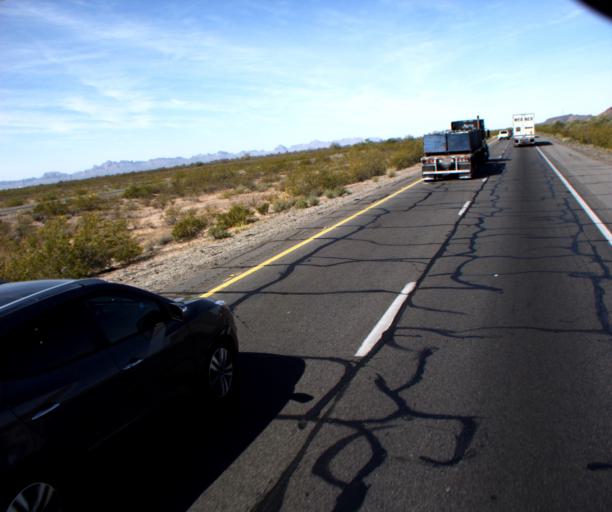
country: US
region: Arizona
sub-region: Maricopa County
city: Buckeye
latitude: 33.5146
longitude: -113.0324
